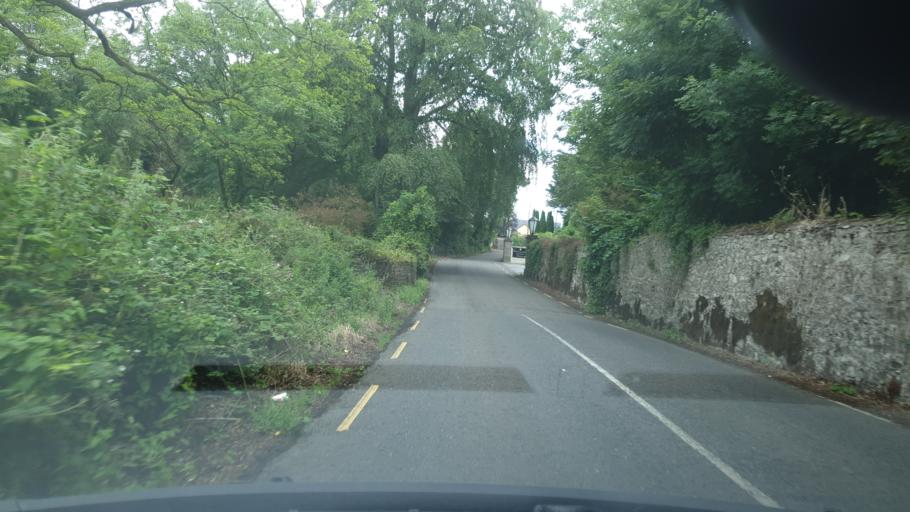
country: IE
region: Munster
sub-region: Ciarrai
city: Tralee
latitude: 52.2552
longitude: -9.6427
